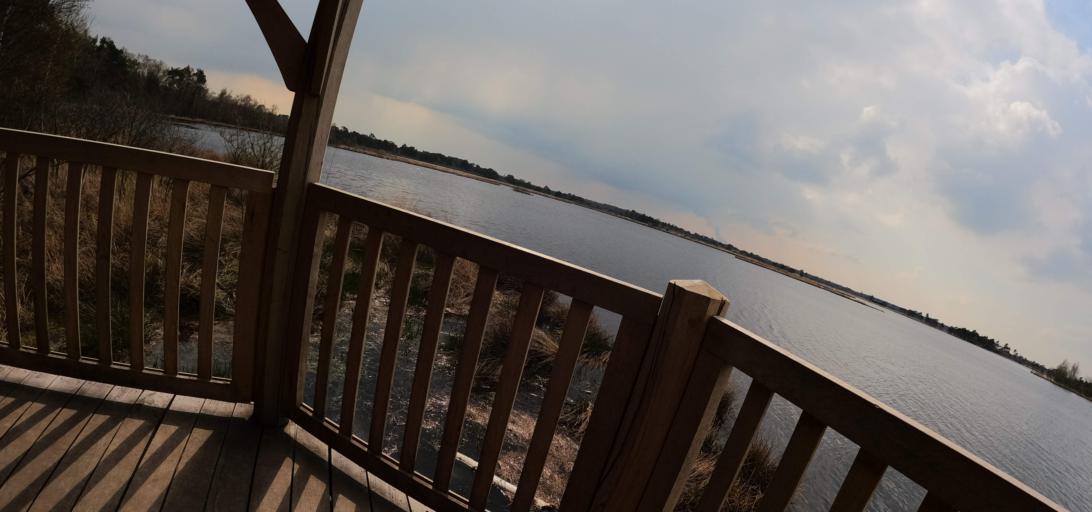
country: BE
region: Flanders
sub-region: Provincie Antwerpen
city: Kalmthout
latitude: 51.4089
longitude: 4.4470
